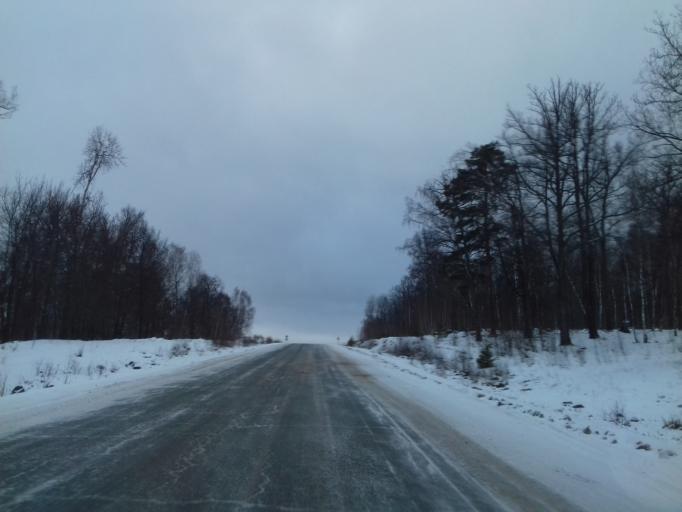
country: RU
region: Bashkortostan
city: Starosubkhangulovo
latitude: 53.2617
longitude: 57.5095
